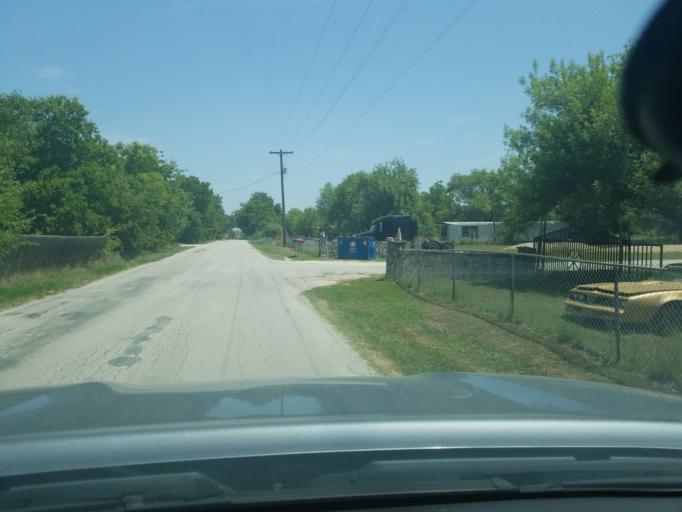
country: US
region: Texas
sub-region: Guadalupe County
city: Cibolo
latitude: 29.5766
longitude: -98.1958
